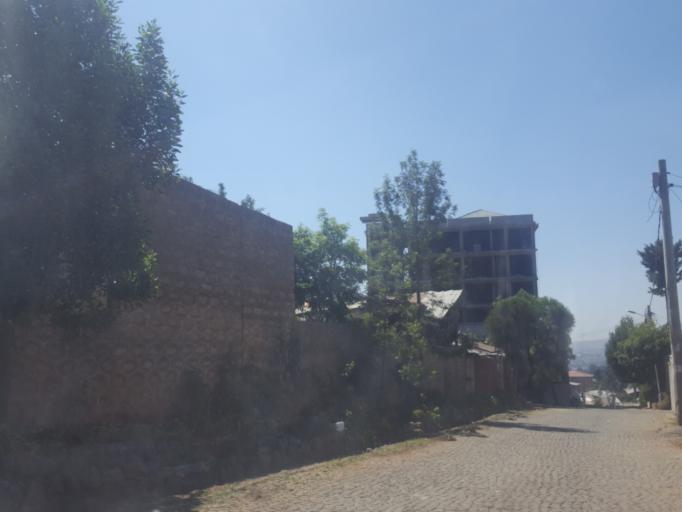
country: ET
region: Adis Abeba
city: Addis Ababa
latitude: 9.0589
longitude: 38.7258
